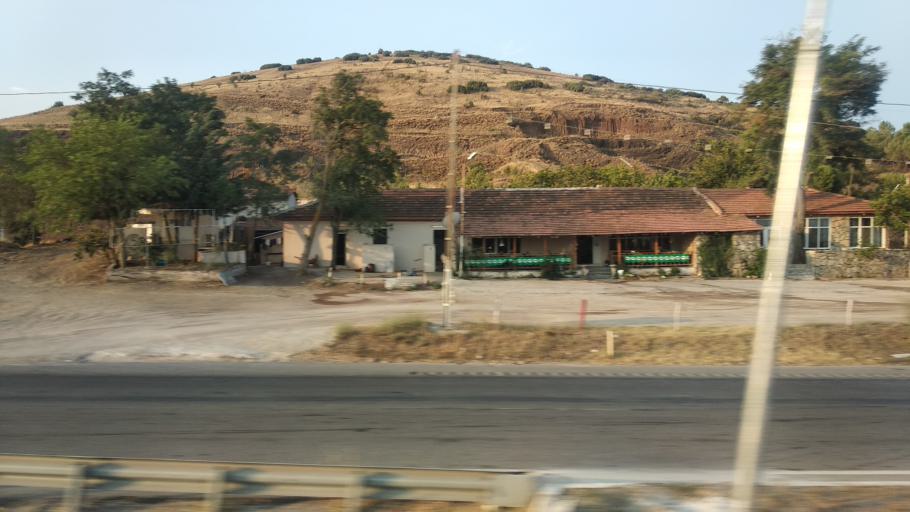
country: TR
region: Manisa
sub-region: Kula
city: Kula
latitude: 38.5674
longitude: 28.5802
